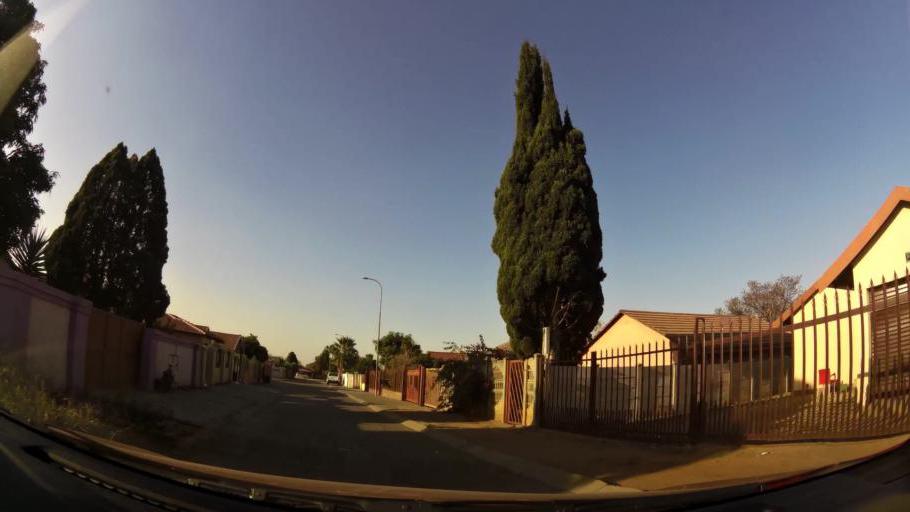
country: ZA
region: North-West
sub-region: Bojanala Platinum District Municipality
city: Rustenburg
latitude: -25.6461
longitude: 27.2258
